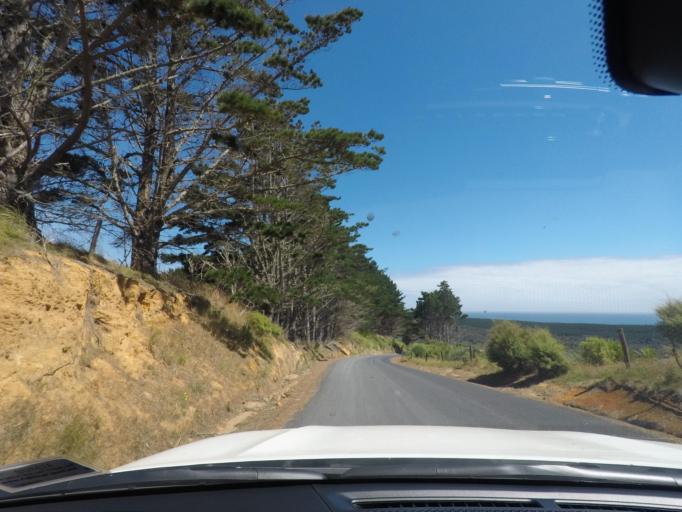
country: NZ
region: Auckland
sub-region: Auckland
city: Parakai
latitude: -36.5867
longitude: 174.2871
